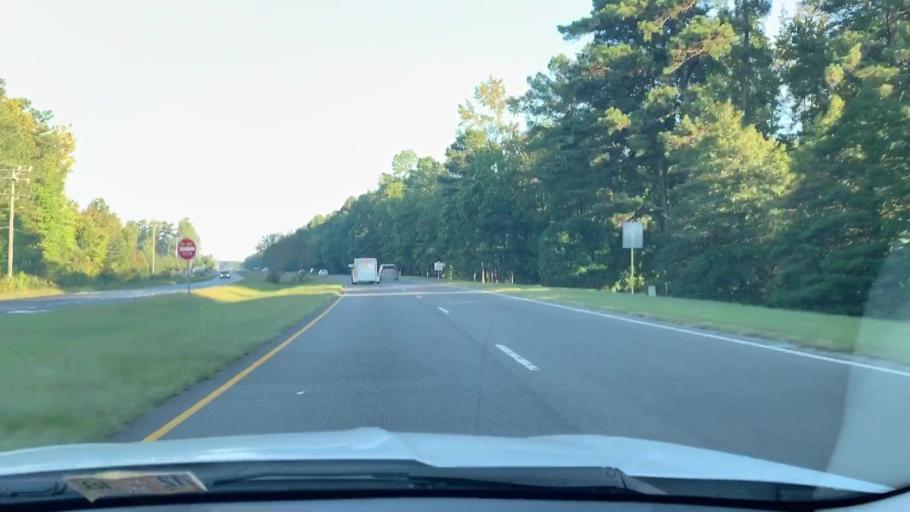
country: US
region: Virginia
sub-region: Gloucester County
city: Gloucester Courthouse
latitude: 37.3338
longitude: -76.5148
